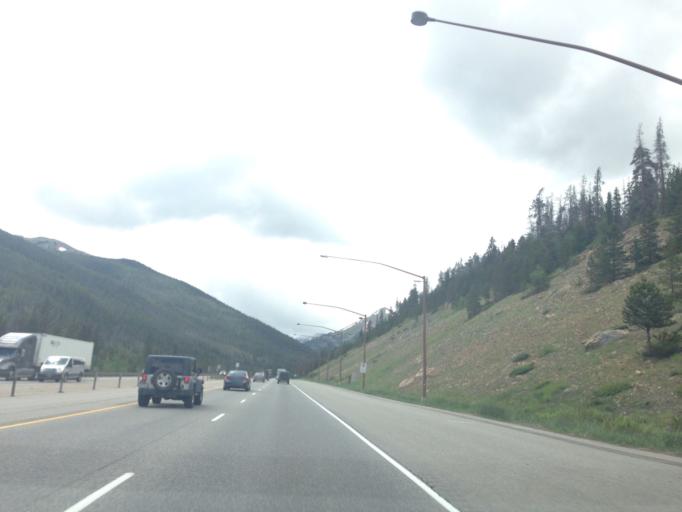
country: US
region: Colorado
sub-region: Clear Creek County
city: Georgetown
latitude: 39.6928
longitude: -105.8155
